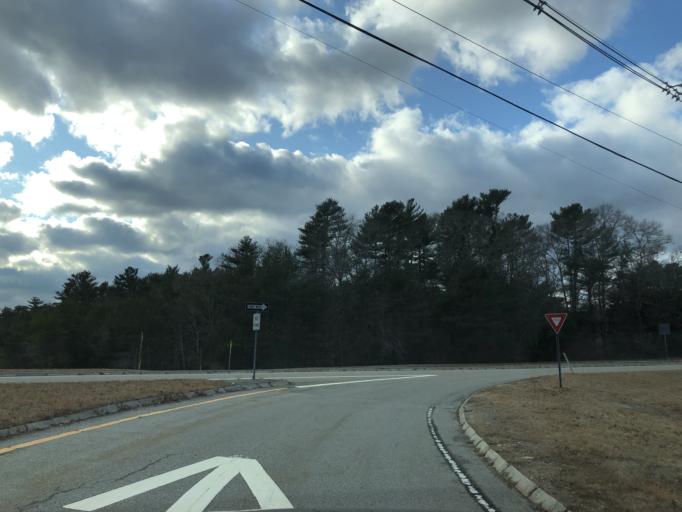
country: US
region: Massachusetts
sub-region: Plymouth County
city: Mattapoisett
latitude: 41.6761
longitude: -70.8238
